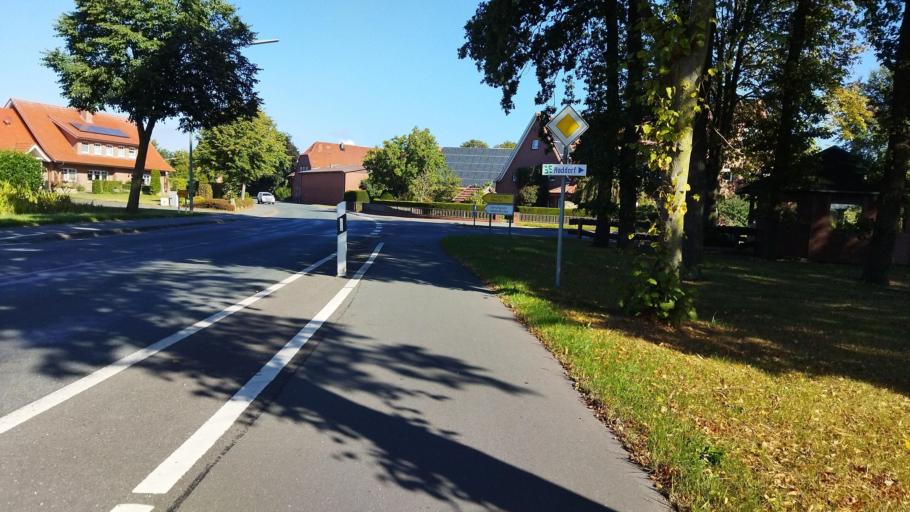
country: DE
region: Lower Saxony
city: Ohne
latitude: 52.2535
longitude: 7.3183
